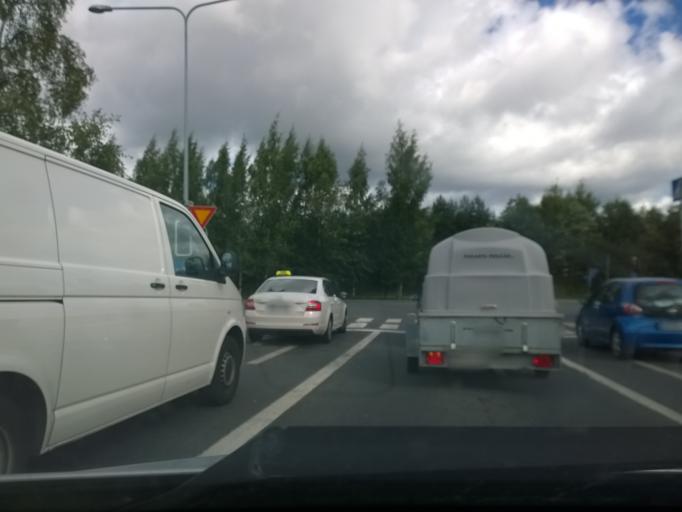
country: FI
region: Pirkanmaa
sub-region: Tampere
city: Tampere
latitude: 61.4773
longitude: 23.8745
